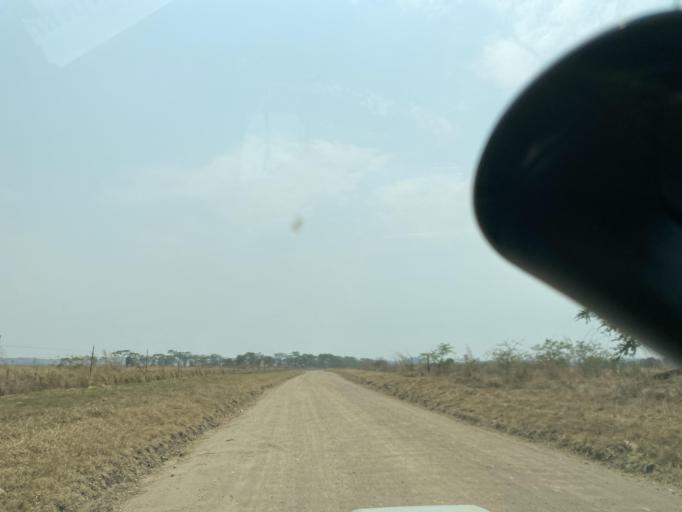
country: ZM
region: Lusaka
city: Kafue
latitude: -15.5841
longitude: 28.1184
